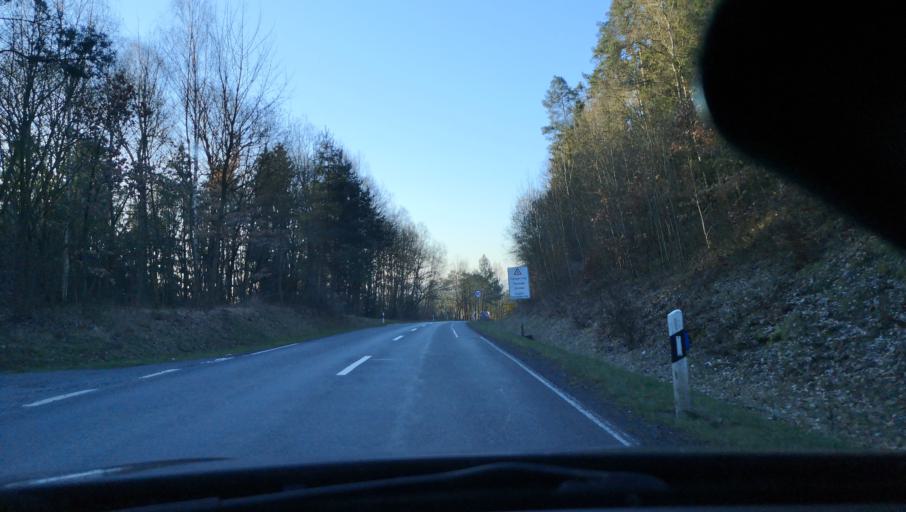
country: DE
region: Bavaria
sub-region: Upper Franconia
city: Sonnefeld
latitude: 50.2315
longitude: 11.1245
